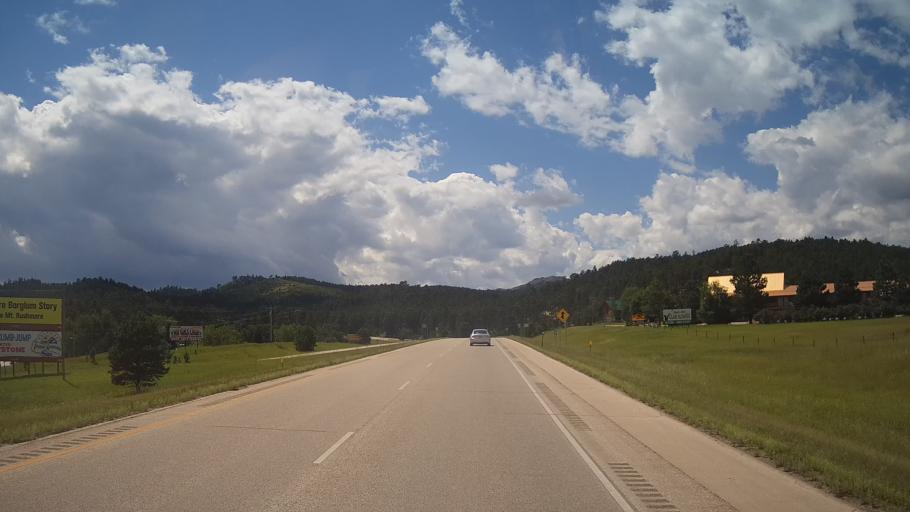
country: US
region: South Dakota
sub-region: Pennington County
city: Colonial Pine Hills
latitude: 43.9599
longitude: -103.3581
